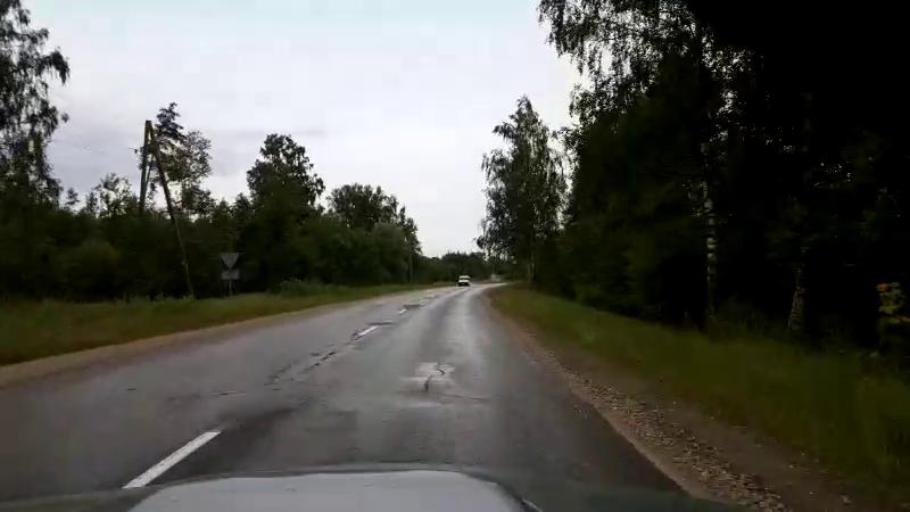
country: LV
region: Kekava
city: Kekava
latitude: 56.7977
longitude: 24.2730
